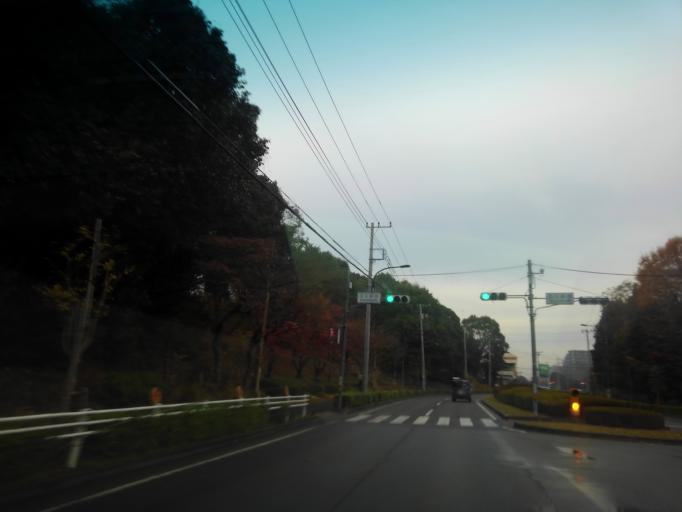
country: JP
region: Tokyo
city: Hino
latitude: 35.6175
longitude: 139.4424
